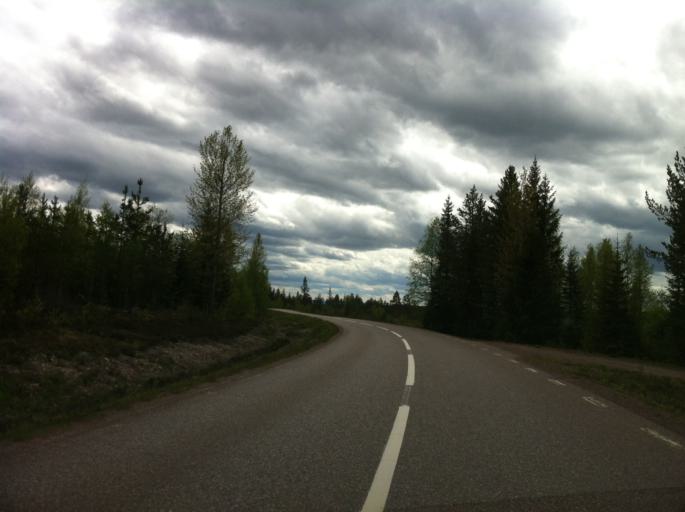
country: NO
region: Hedmark
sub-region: Trysil
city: Innbygda
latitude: 61.5057
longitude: 13.0777
